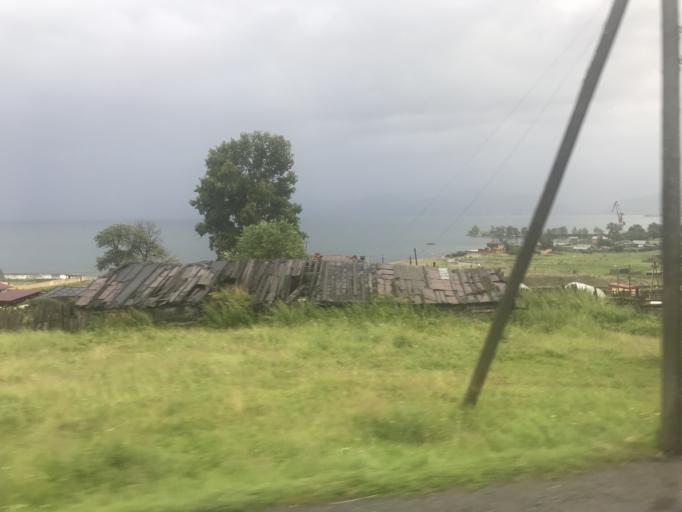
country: RU
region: Irkutsk
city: Kultuk
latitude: 51.7297
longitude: 103.7180
